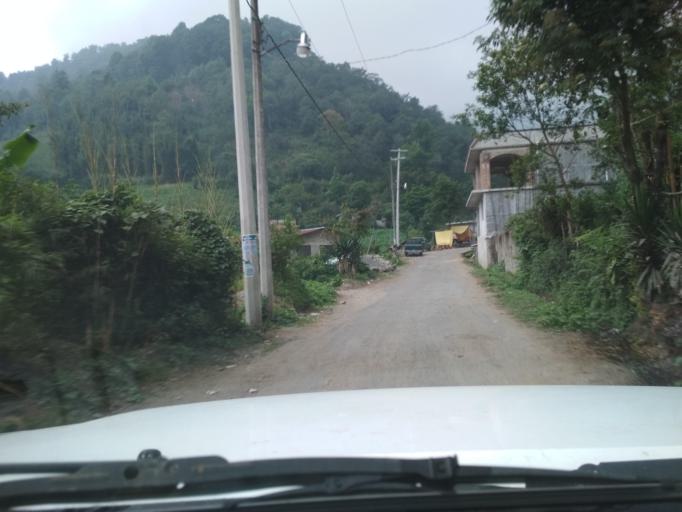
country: MX
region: Veracruz
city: La Perla
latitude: 18.9295
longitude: -97.1420
